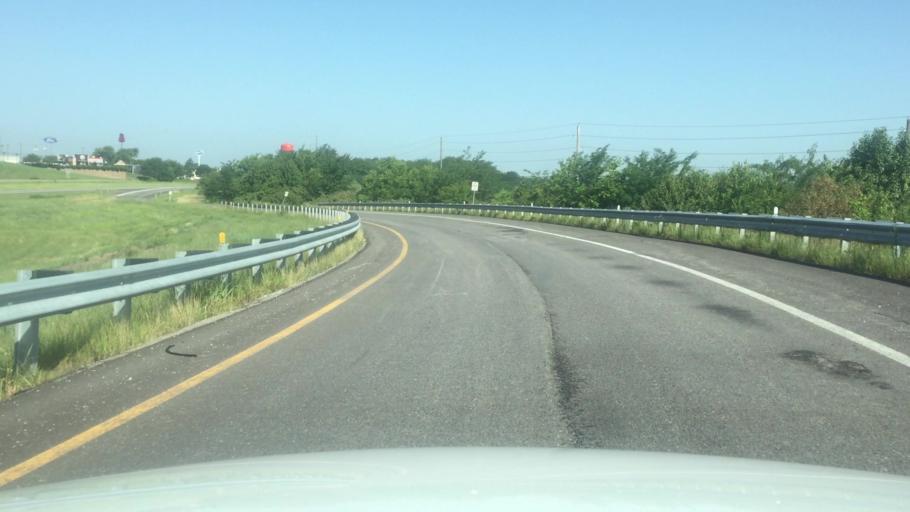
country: US
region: Missouri
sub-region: Platte County
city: Platte City
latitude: 39.3543
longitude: -94.7608
